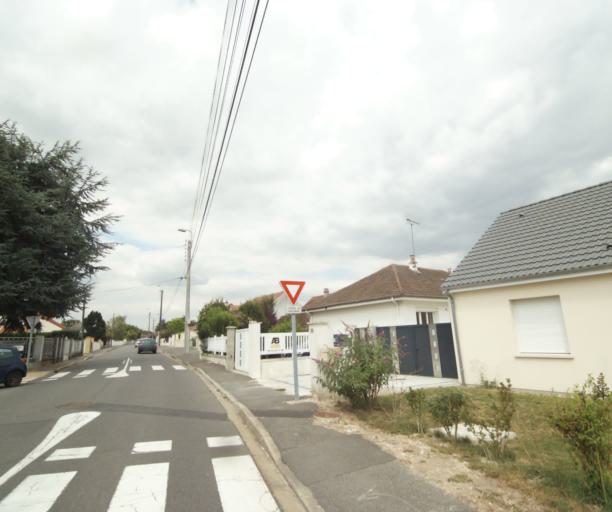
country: FR
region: Centre
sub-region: Departement du Loiret
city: Saran
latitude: 47.9373
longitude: 1.8690
